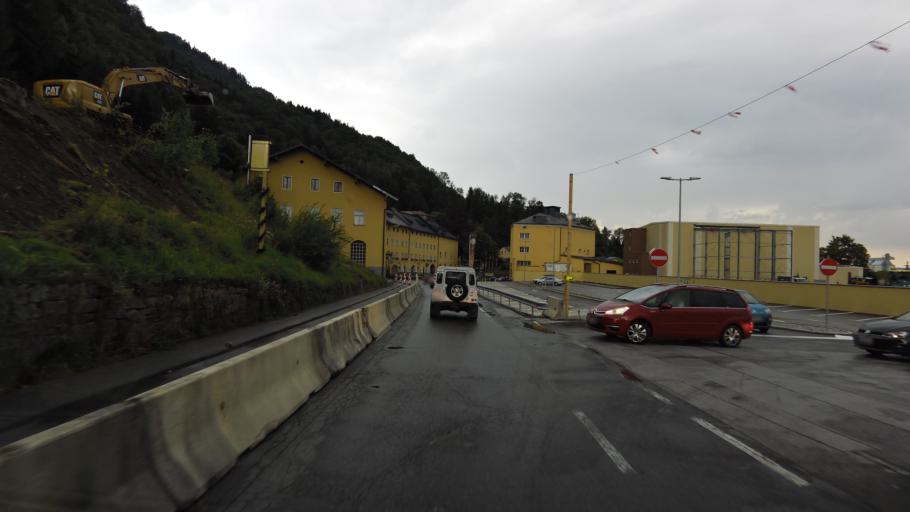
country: AT
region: Salzburg
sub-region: Politischer Bezirk Hallein
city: Oberalm
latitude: 47.6934
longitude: 13.0797
